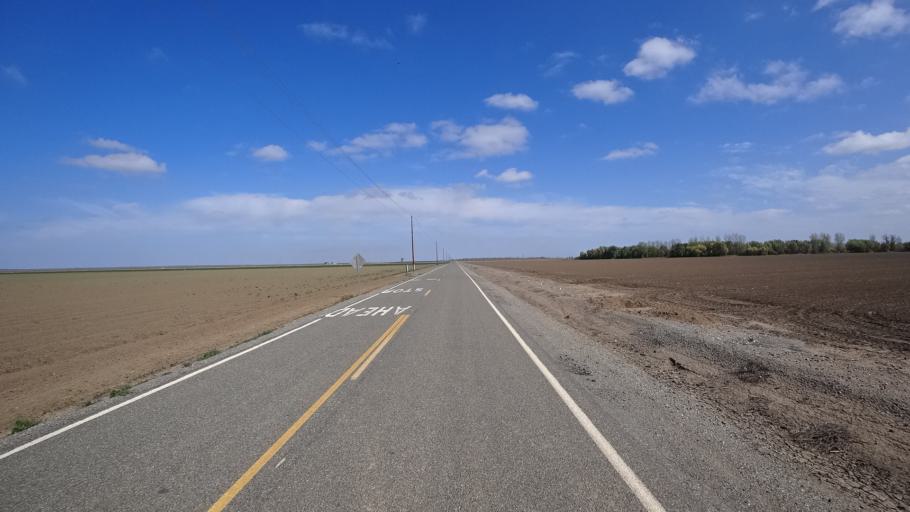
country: US
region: California
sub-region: Butte County
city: Biggs
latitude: 39.4219
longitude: -121.9294
